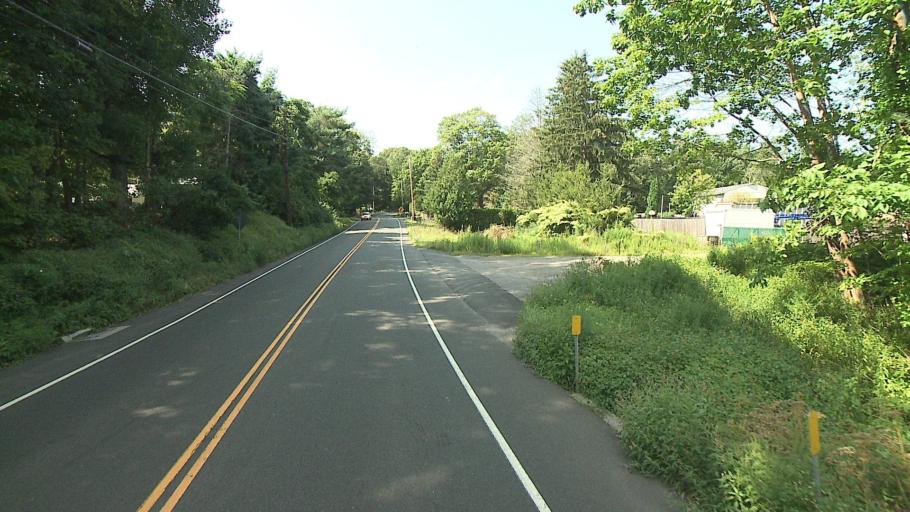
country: US
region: Connecticut
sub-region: Fairfield County
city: Newtown
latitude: 41.4575
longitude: -73.3830
